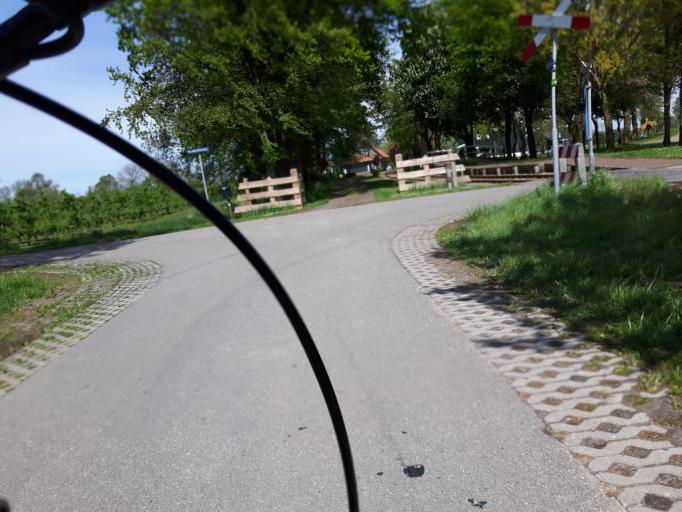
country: NL
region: Zeeland
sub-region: Gemeente Goes
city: Goes
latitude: 51.4536
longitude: 3.8798
